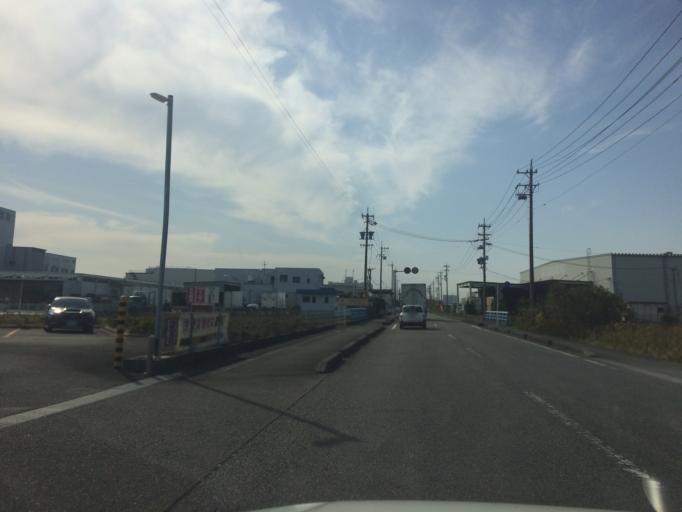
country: JP
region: Shizuoka
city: Fujieda
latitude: 34.7856
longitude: 138.2893
